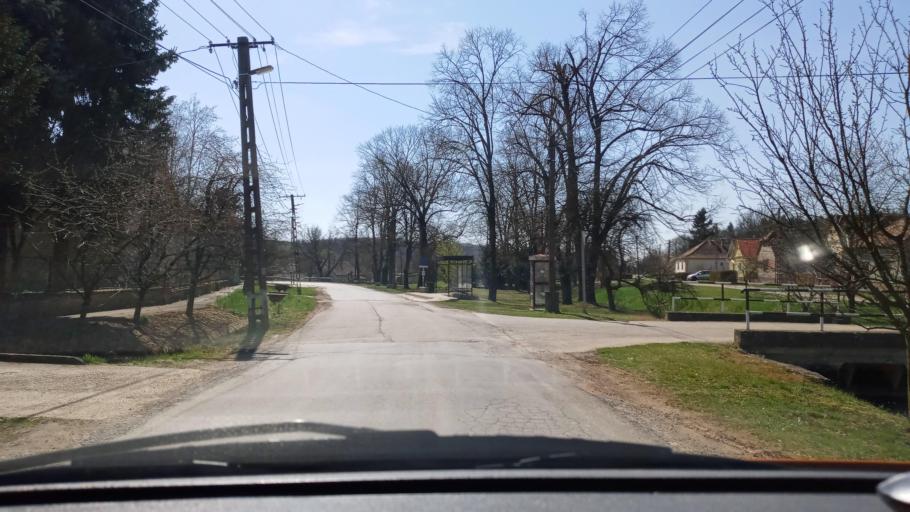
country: HU
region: Baranya
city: Pecsvarad
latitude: 46.0592
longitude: 18.4515
